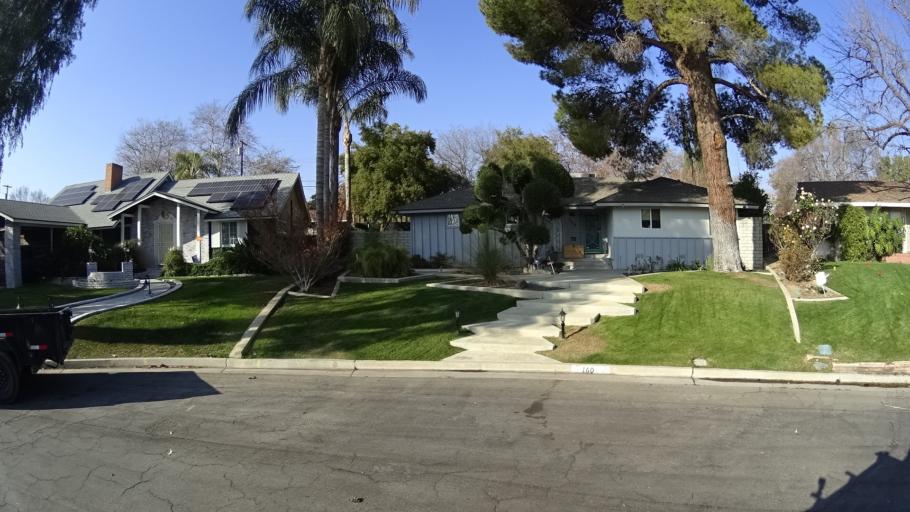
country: US
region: California
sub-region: Kern County
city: Oildale
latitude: 35.4029
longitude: -118.9996
